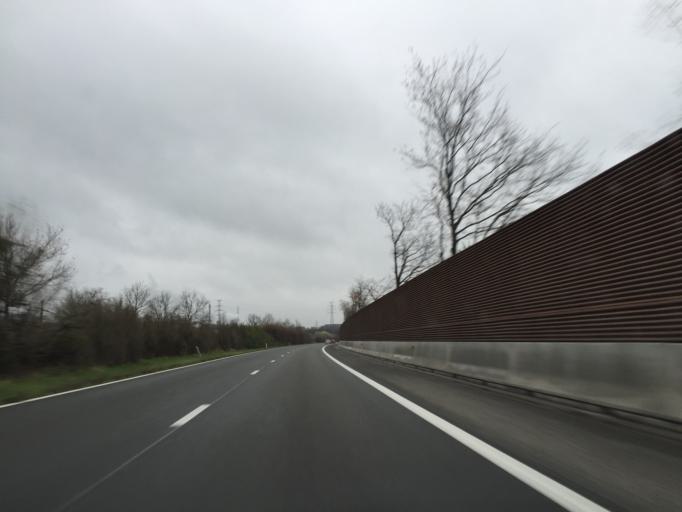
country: BE
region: Flanders
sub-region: Provincie Oost-Vlaanderen
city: Evergem
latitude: 51.1170
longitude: 3.7287
